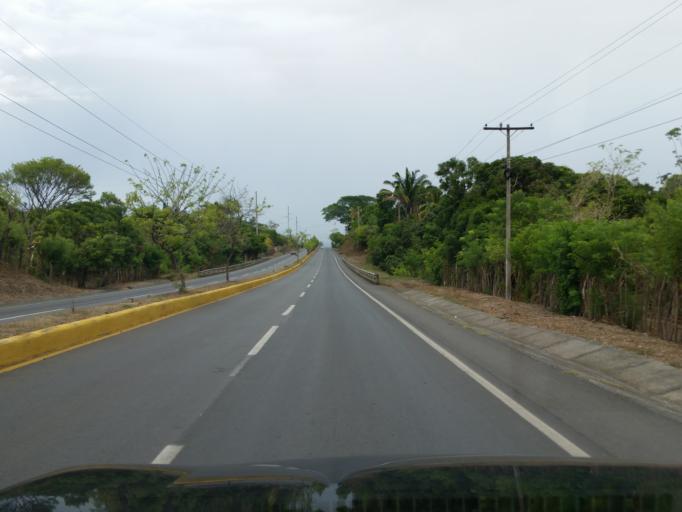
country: NI
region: Masaya
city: Masaya
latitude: 11.9751
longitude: -86.0619
